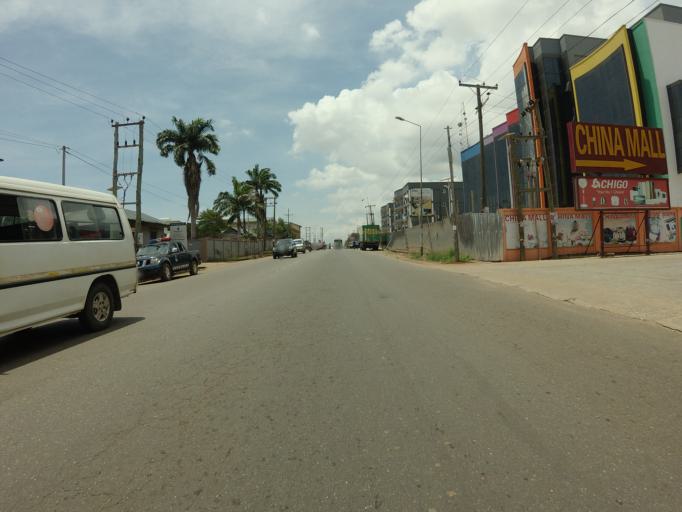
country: GH
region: Greater Accra
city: Medina Estates
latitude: 5.6386
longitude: -0.1242
